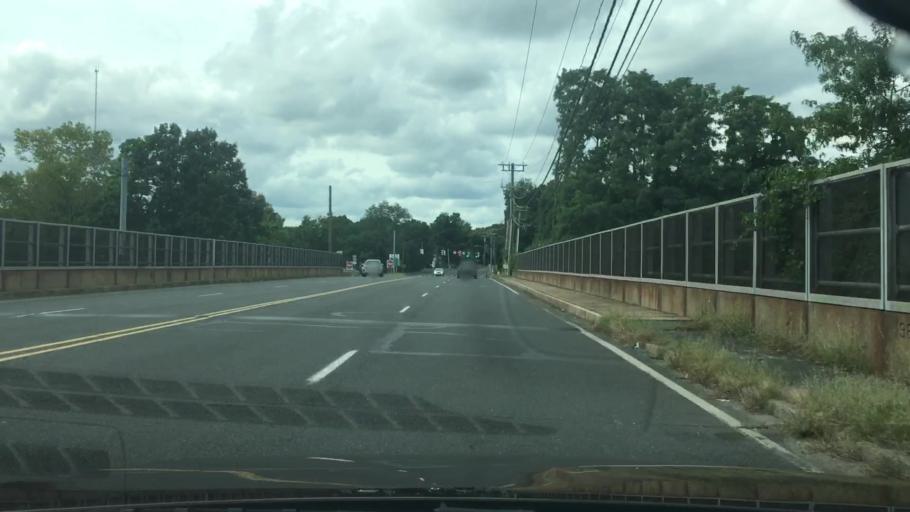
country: US
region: Connecticut
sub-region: Hartford County
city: Farmington
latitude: 41.7069
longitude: -72.8016
